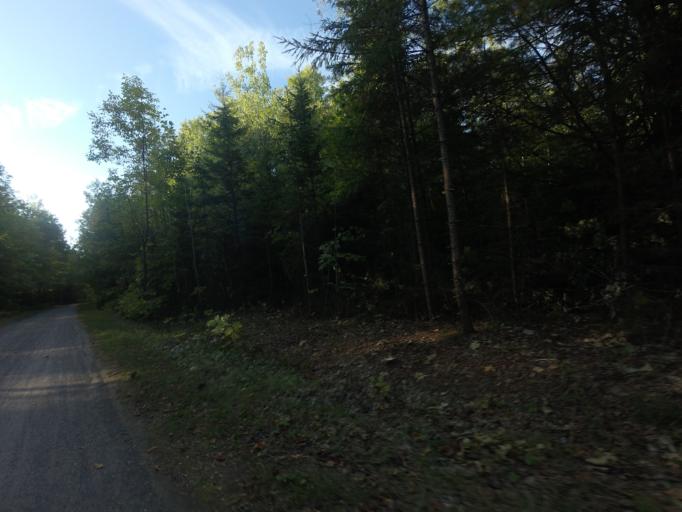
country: CA
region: Quebec
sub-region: Laurentides
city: Saint-Jerome
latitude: 45.8159
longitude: -74.0460
